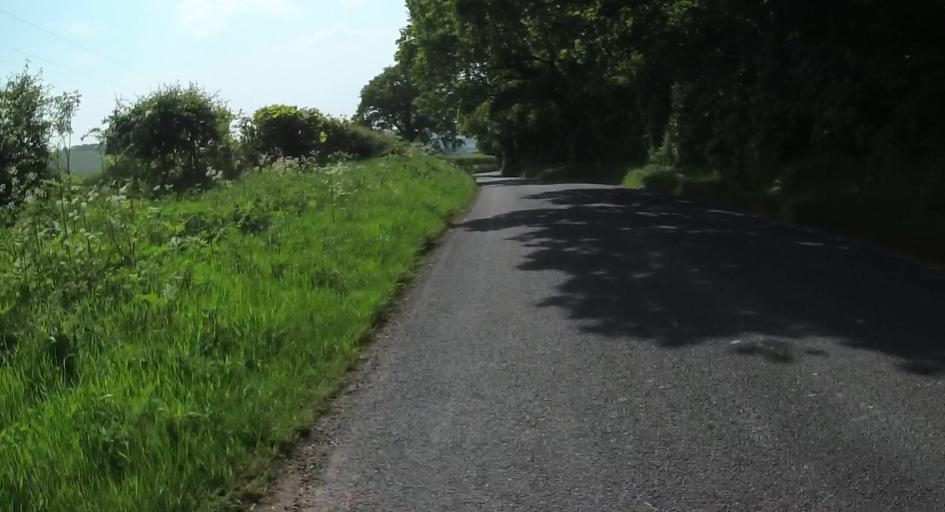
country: GB
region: England
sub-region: Hampshire
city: Kingsclere
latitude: 51.3188
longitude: -1.2790
